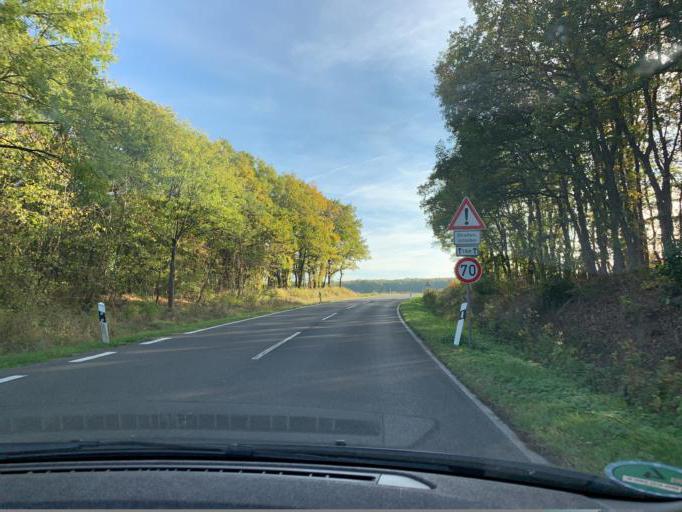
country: DE
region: North Rhine-Westphalia
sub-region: Regierungsbezirk Koln
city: Kreuzau
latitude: 50.7194
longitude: 6.5178
